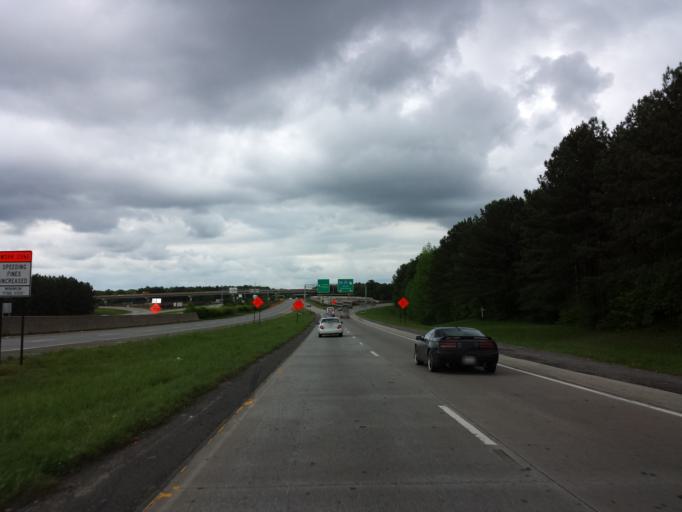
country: US
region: Georgia
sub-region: Cobb County
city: Marietta
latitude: 33.9800
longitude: -84.5471
